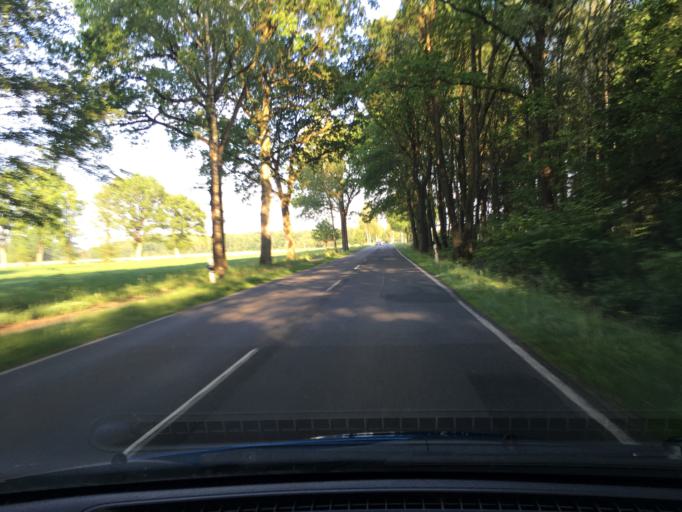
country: DE
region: Lower Saxony
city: Otter
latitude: 53.2549
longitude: 9.7538
